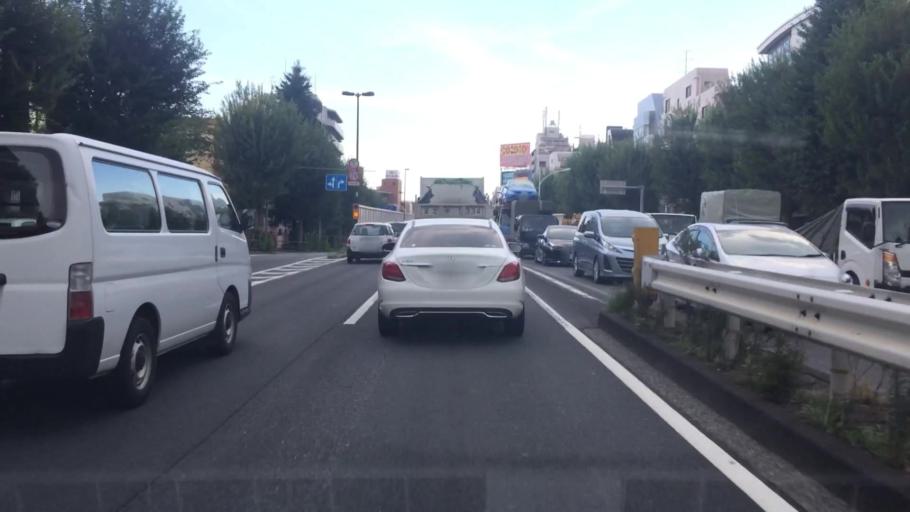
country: JP
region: Tokyo
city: Tokyo
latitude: 35.7001
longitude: 139.6547
